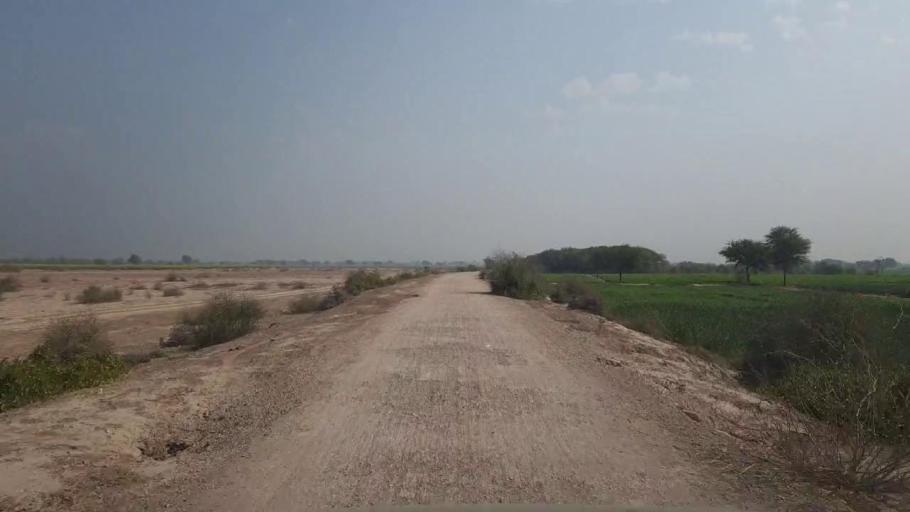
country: PK
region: Sindh
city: Hala
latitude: 25.7638
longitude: 68.4232
